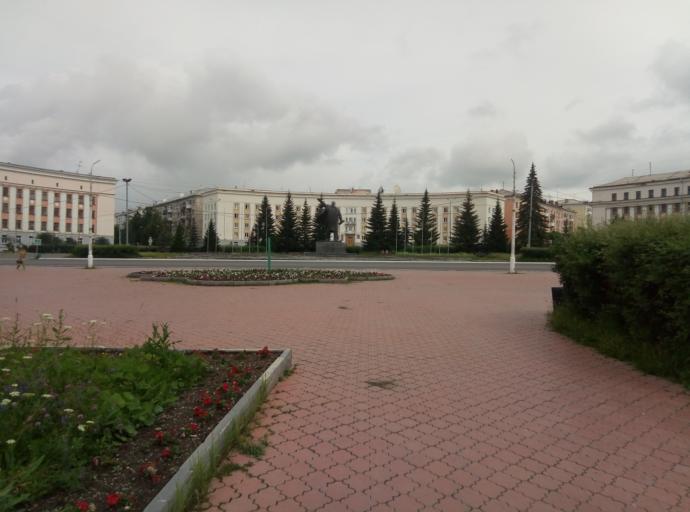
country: RU
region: Sverdlovsk
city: Krasnotur'insk
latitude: 59.7633
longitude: 60.1936
